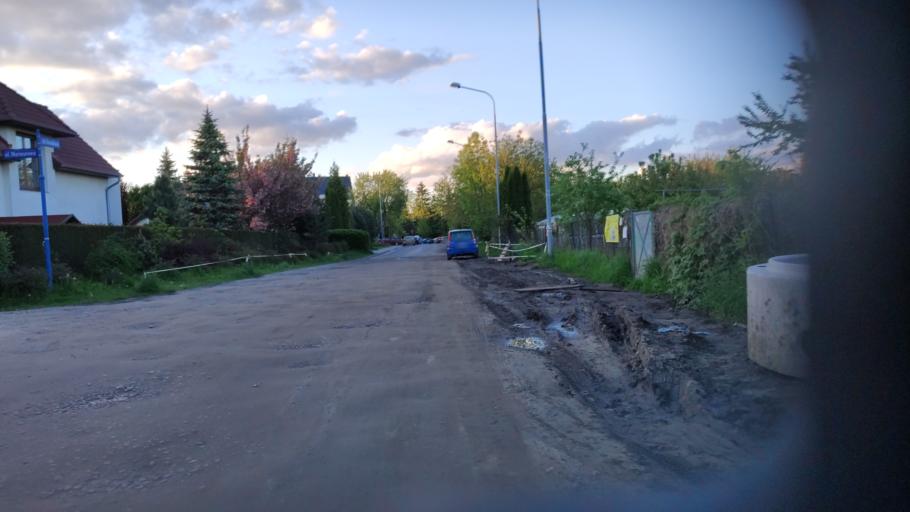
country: PL
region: Lower Silesian Voivodeship
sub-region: Powiat wroclawski
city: Wroclaw
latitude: 51.0673
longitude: 17.0410
